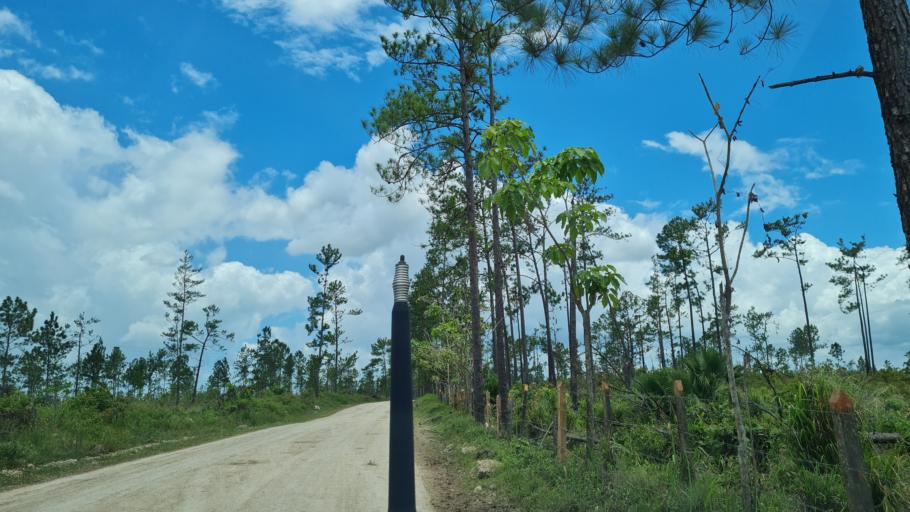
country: NI
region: Atlantico Sur
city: La Cruz de Rio Grande
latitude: 13.5704
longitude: -84.3206
